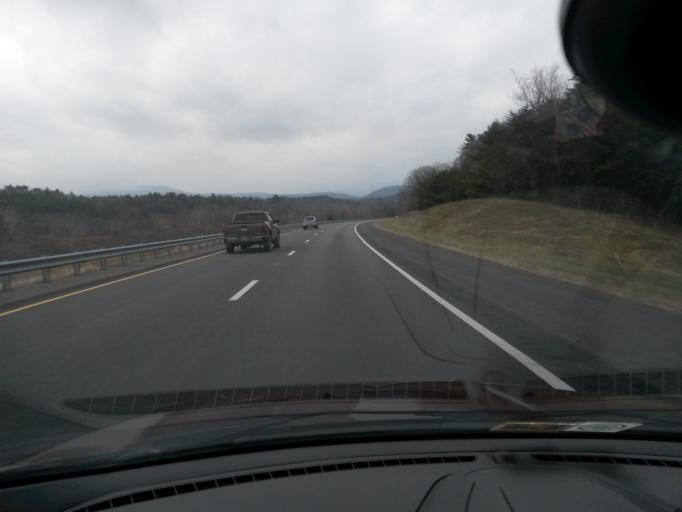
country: US
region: Virginia
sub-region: Alleghany County
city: Clifton Forge
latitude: 37.7959
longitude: -79.7234
